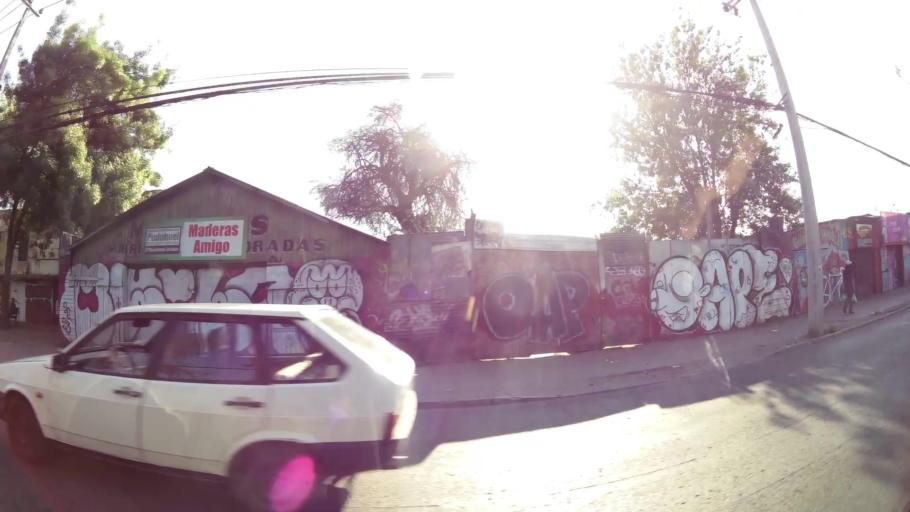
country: CL
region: Santiago Metropolitan
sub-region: Provincia de Santiago
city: Santiago
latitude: -33.3881
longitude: -70.6423
